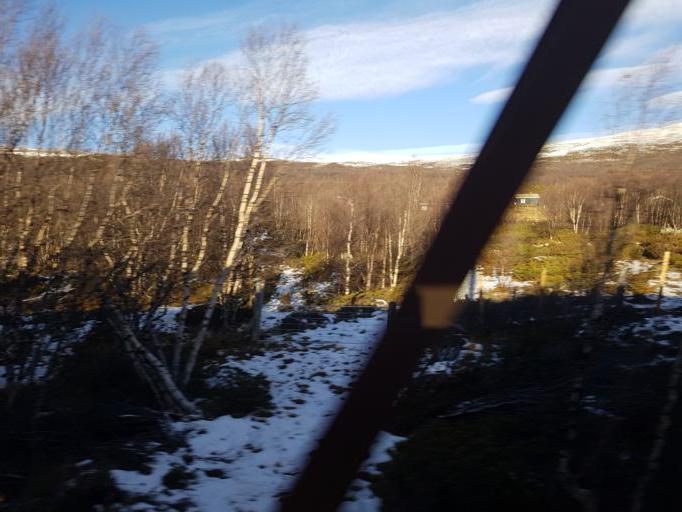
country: NO
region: Oppland
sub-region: Dovre
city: Dovre
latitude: 62.1878
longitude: 9.4777
